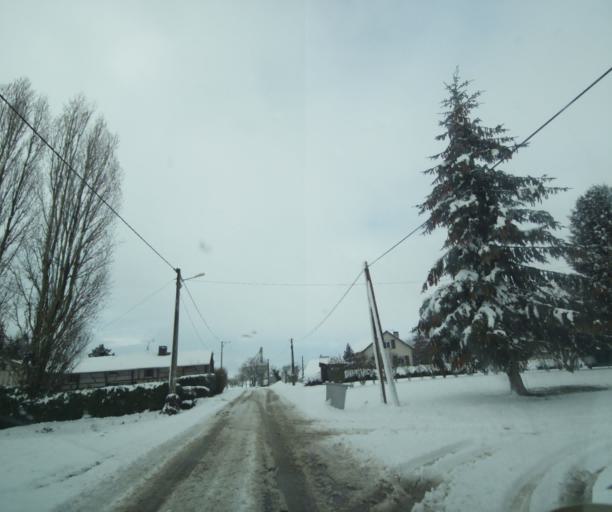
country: FR
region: Champagne-Ardenne
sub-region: Departement de la Haute-Marne
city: Montier-en-Der
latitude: 48.5250
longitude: 4.7123
